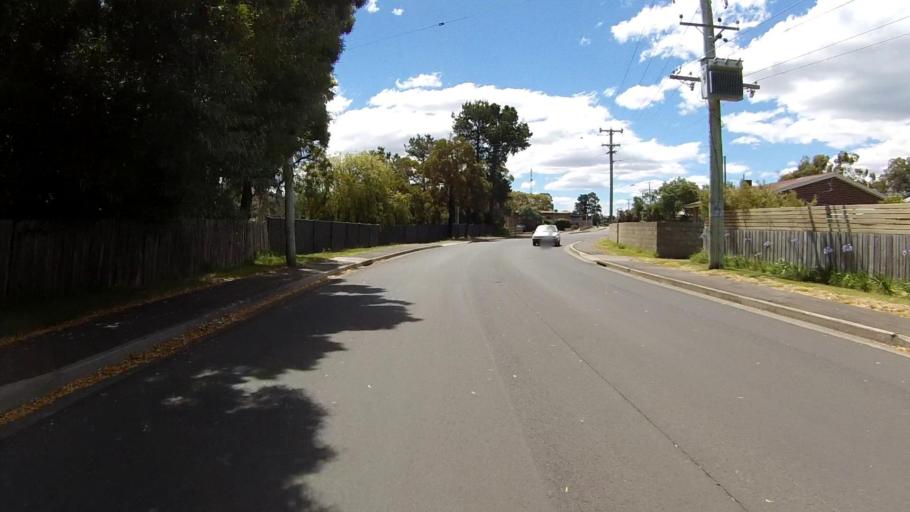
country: AU
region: Tasmania
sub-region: Clarence
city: Lauderdale
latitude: -42.9107
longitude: 147.4921
